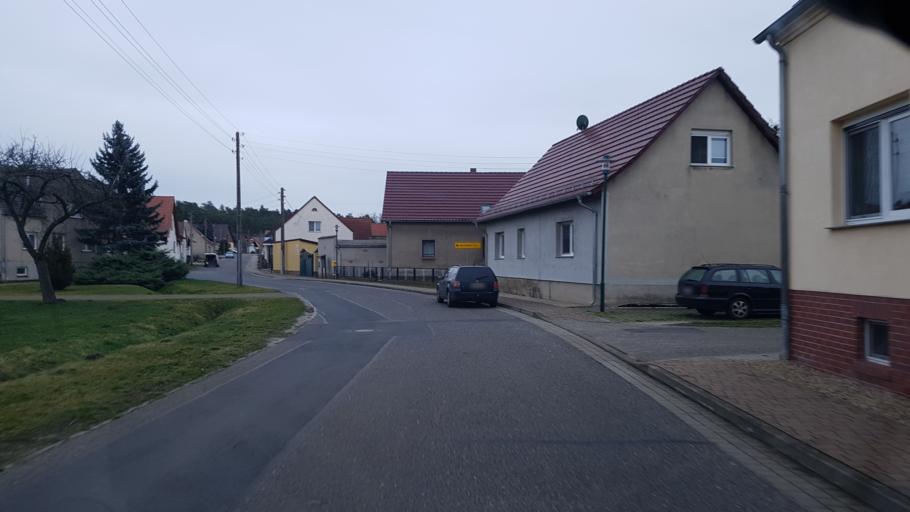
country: DE
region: Brandenburg
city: Schlieben
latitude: 51.7123
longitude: 13.3004
